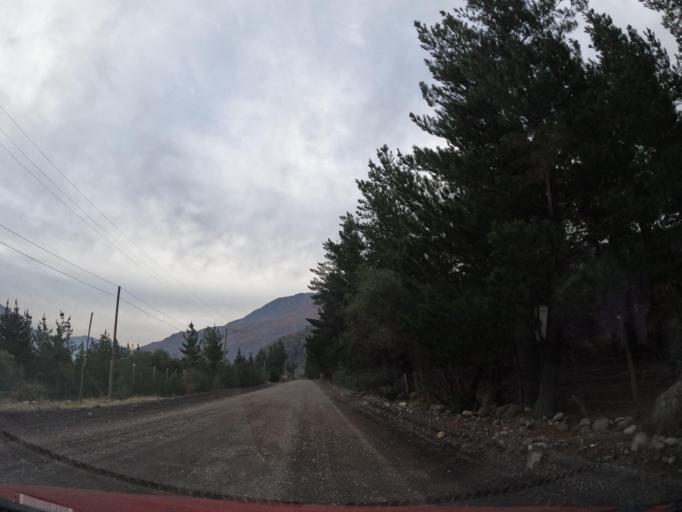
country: CL
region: Maule
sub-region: Provincia de Linares
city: Colbun
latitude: -35.7038
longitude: -71.0959
